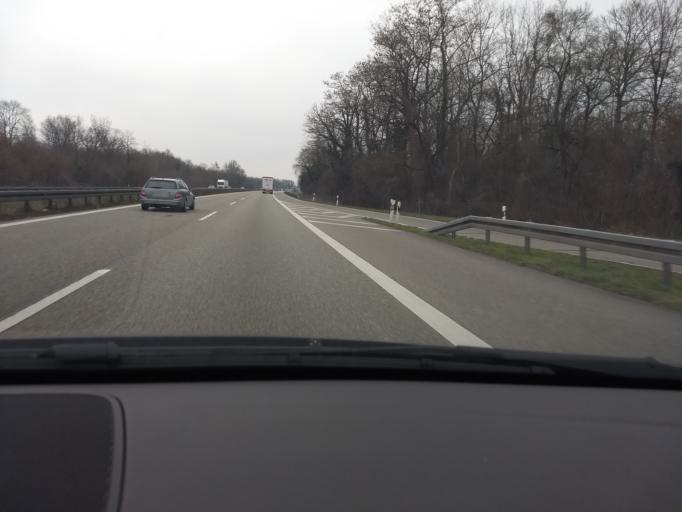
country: DE
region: Baden-Wuerttemberg
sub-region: Freiburg Region
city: Hartheim
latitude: 47.9233
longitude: 7.5983
